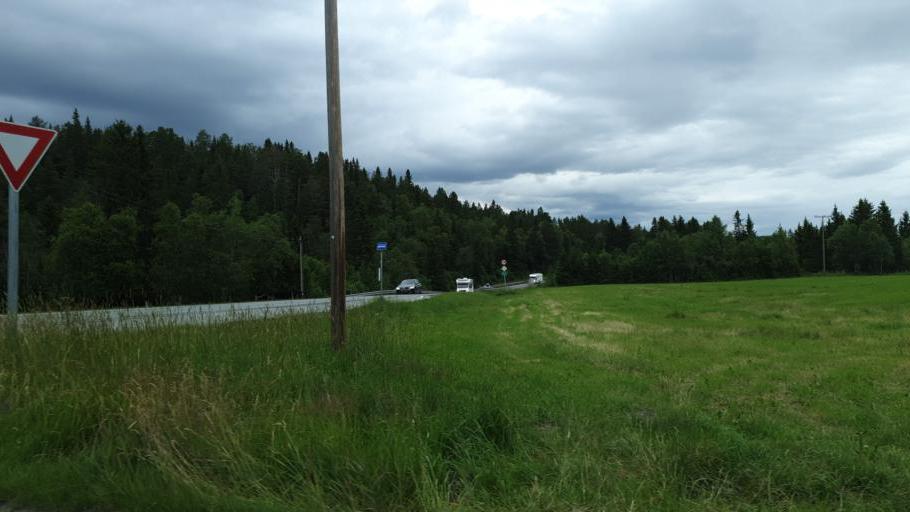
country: NO
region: Sor-Trondelag
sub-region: Rennebu
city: Berkak
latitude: 62.8910
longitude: 10.1022
